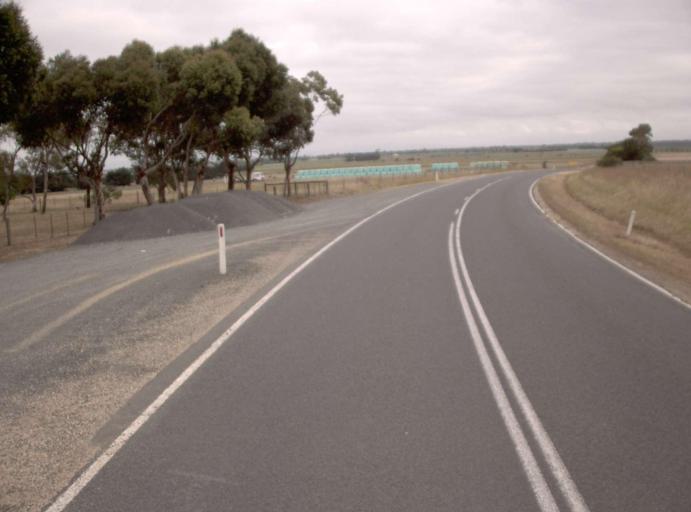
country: AU
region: Victoria
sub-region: Wellington
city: Sale
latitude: -38.0936
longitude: 146.9863
